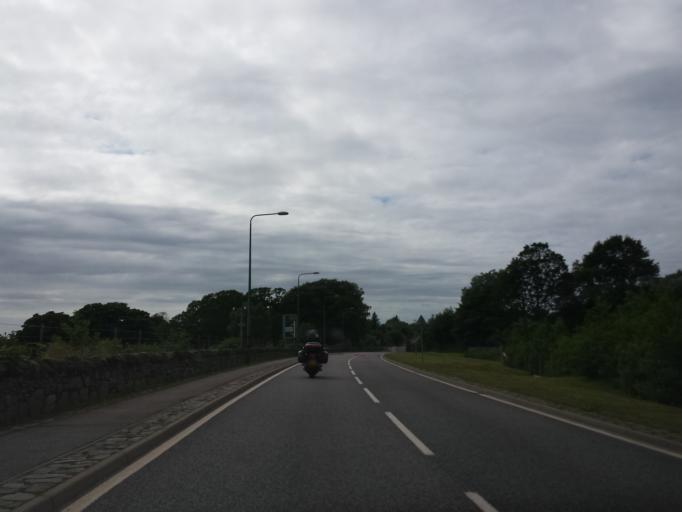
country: GB
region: Scotland
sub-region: Argyll and Bute
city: Isle Of Mull
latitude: 56.9109
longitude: -5.8344
